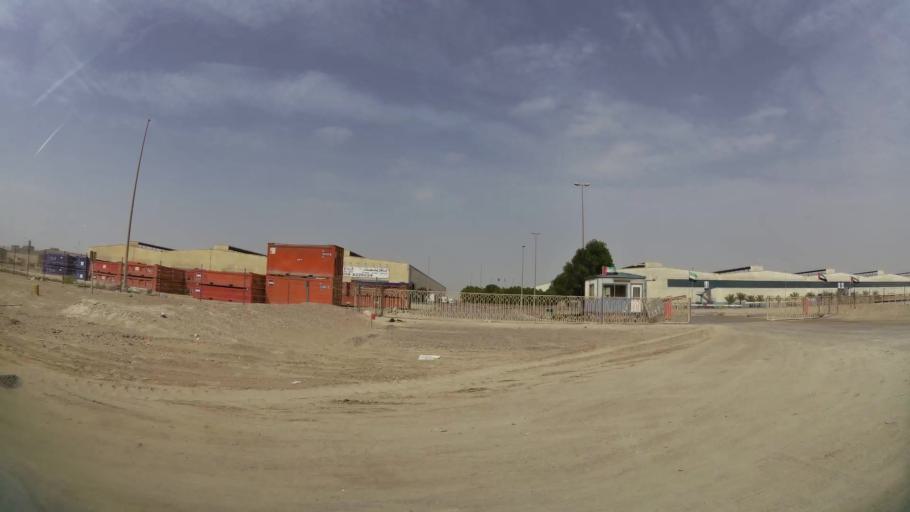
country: AE
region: Abu Dhabi
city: Abu Dhabi
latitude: 24.3286
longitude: 54.4793
